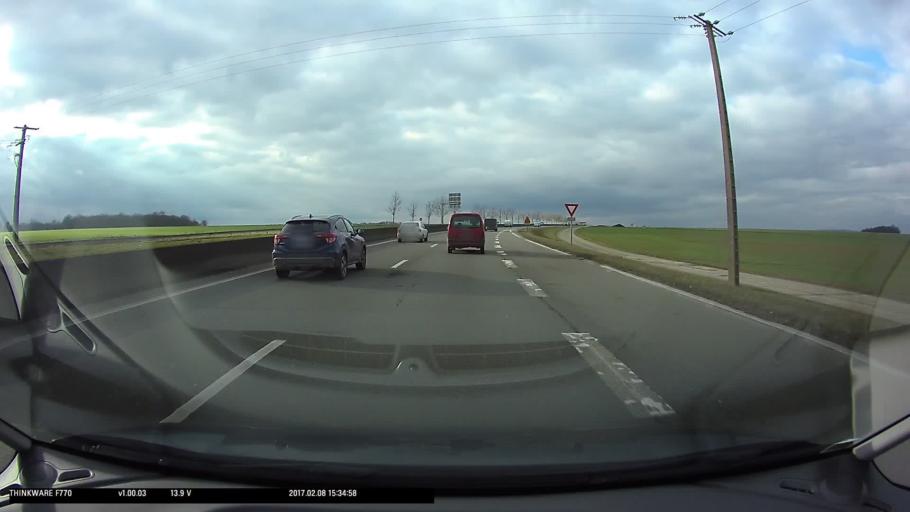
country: FR
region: Ile-de-France
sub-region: Departement du Val-d'Oise
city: Sagy
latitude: 49.0717
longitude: 1.9598
